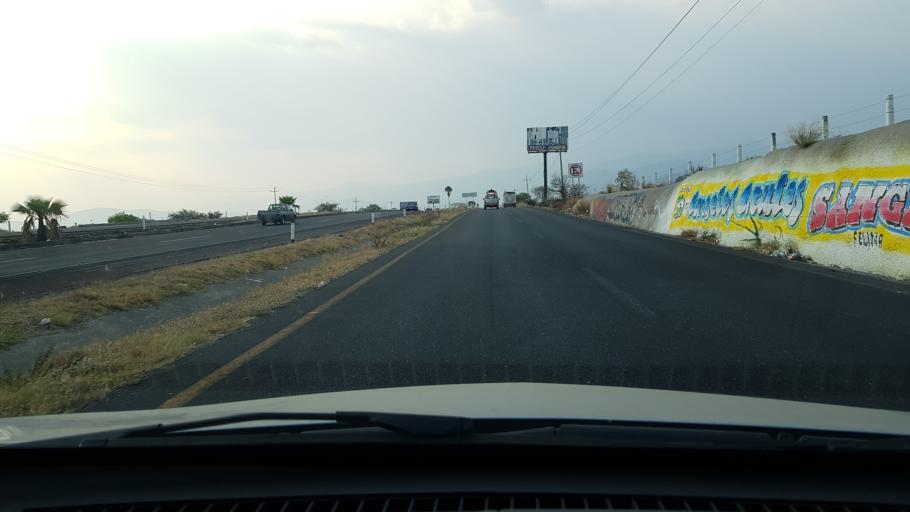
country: MX
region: Morelos
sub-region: Cuautla
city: Tierra Larga (Campo Nuevo)
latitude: 18.8691
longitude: -98.9532
